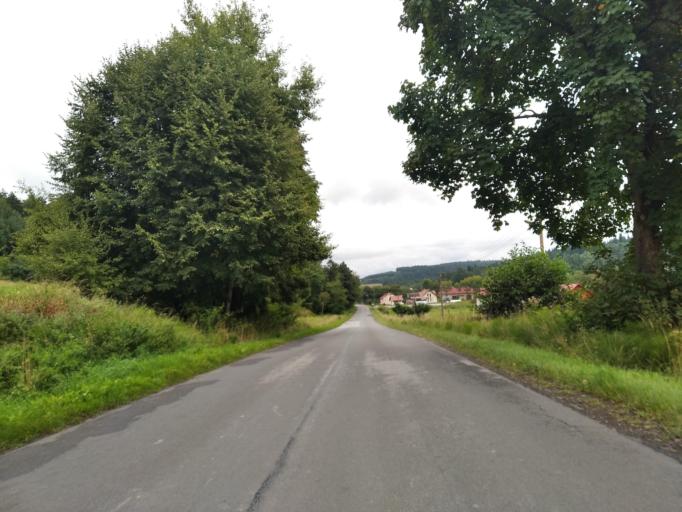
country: PL
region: Subcarpathian Voivodeship
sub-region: Powiat przemyski
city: Bircza
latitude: 49.6913
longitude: 22.4352
